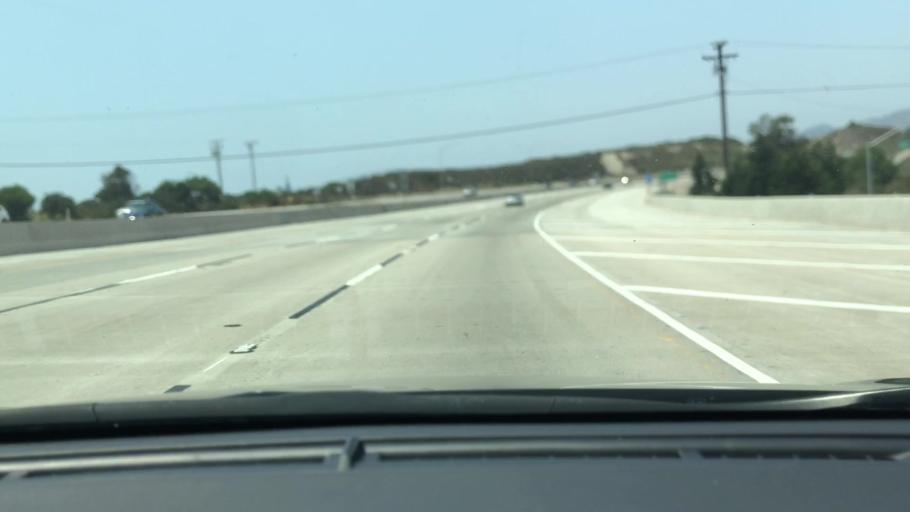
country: US
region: California
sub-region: Santa Barbara County
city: Carpinteria
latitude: 34.3764
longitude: -119.4776
